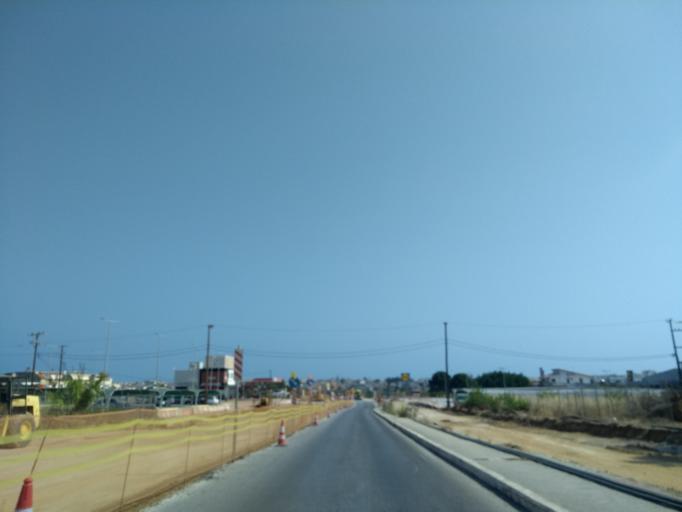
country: GR
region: Crete
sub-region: Nomos Chanias
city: Mournies
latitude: 35.4961
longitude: 24.0182
